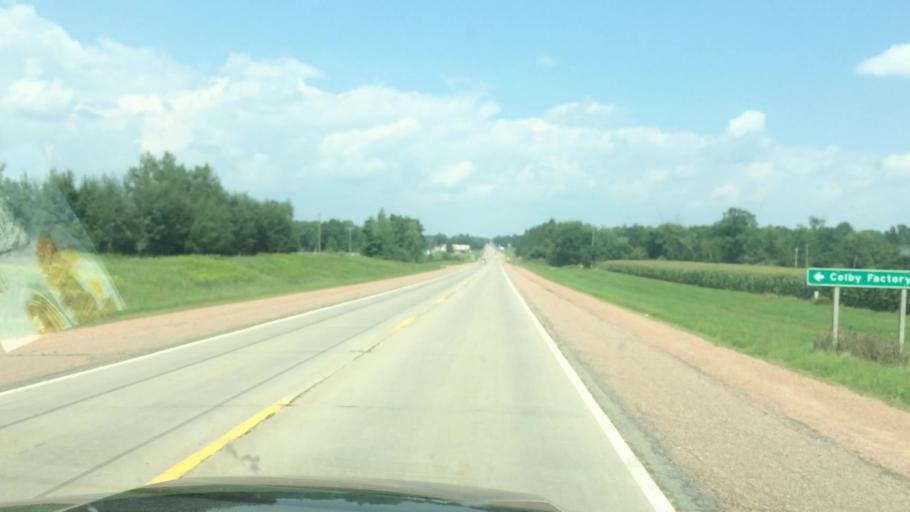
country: US
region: Wisconsin
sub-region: Clark County
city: Colby
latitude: 44.8858
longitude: -90.3154
